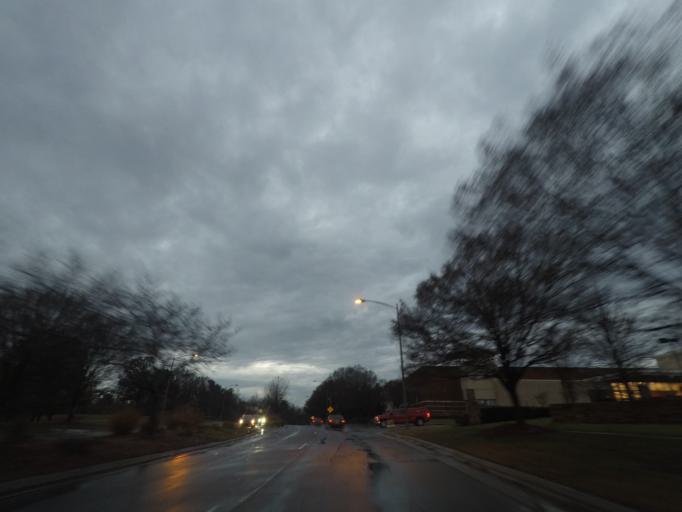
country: US
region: North Carolina
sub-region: Orange County
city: Chapel Hill
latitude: 35.9026
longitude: -78.9551
